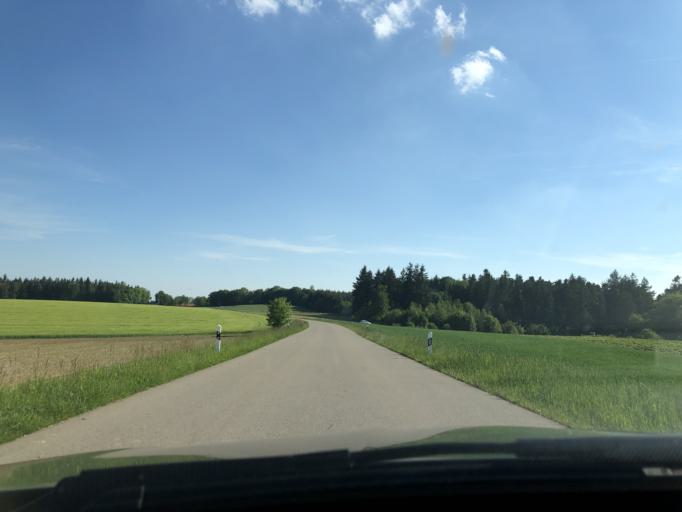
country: DE
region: Bavaria
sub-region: Upper Bavaria
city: Kirchdorf
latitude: 48.4356
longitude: 11.6791
